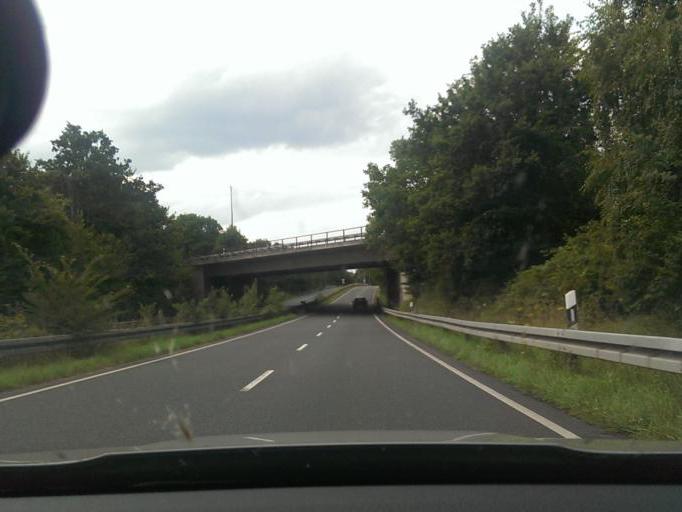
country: DE
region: Lower Saxony
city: Hannover
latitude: 52.3888
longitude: 9.6869
